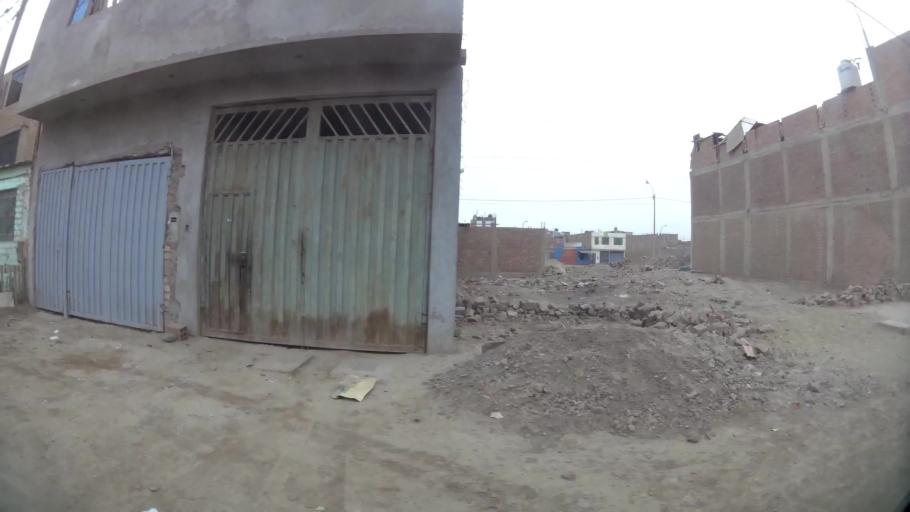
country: PE
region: Lima
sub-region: Lima
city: Independencia
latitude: -11.9655
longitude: -77.0947
